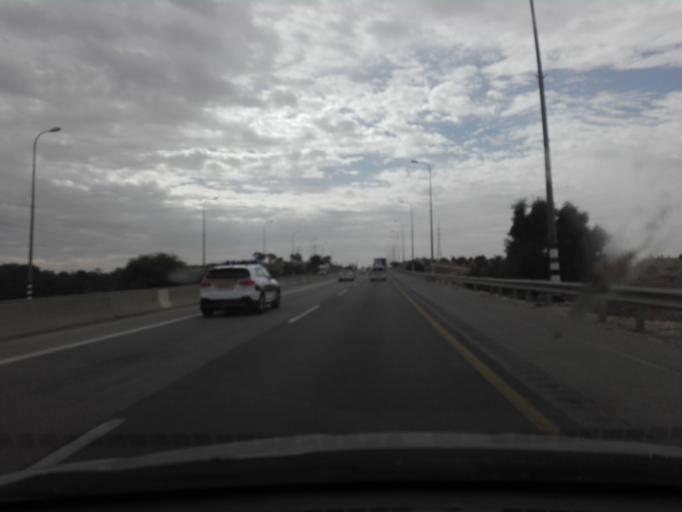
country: IL
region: Southern District
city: Lehavim
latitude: 31.3518
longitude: 34.7926
